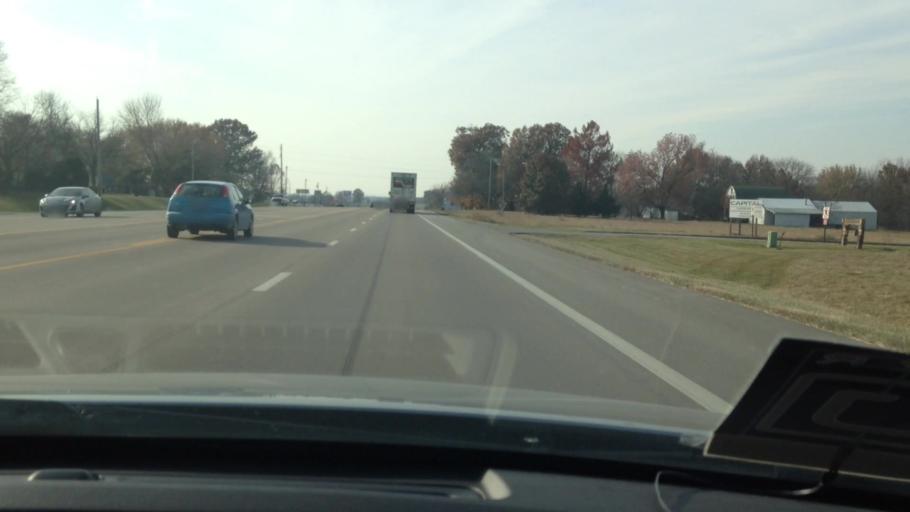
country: US
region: Missouri
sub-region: Henry County
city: Clinton
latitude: 38.3895
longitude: -93.8031
